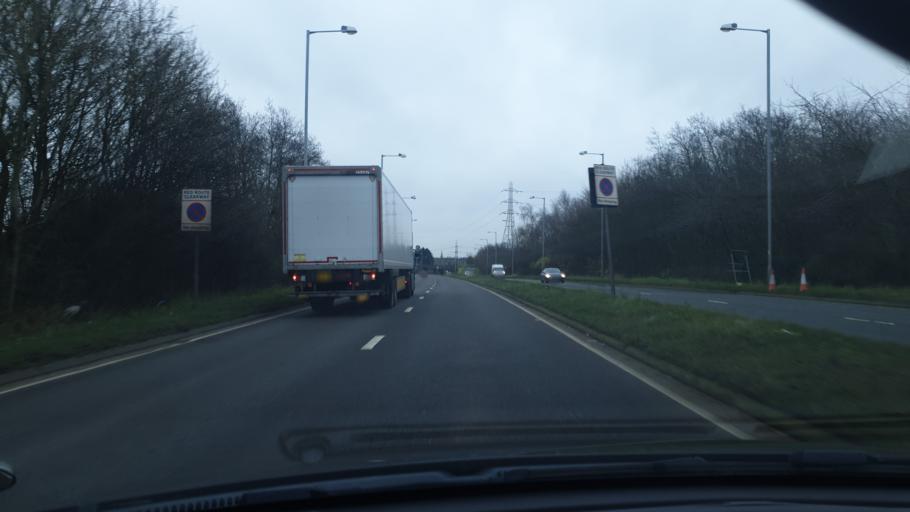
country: GB
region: England
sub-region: Walsall
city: Willenhall
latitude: 52.5797
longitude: -2.0614
